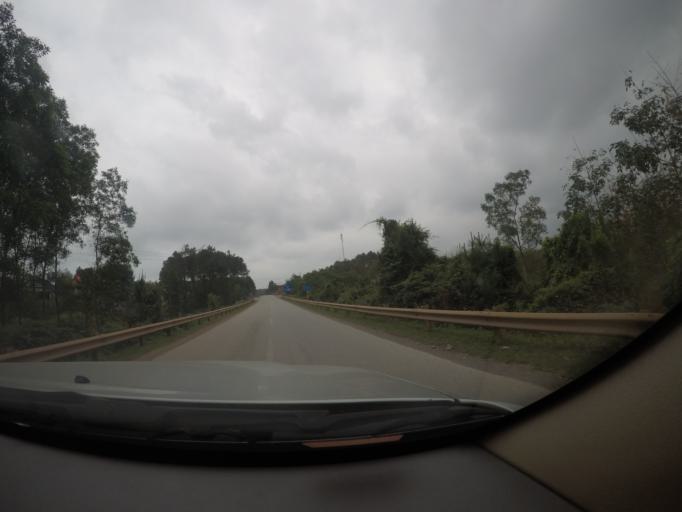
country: VN
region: Quang Binh
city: Kien Giang
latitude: 17.1536
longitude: 106.7499
